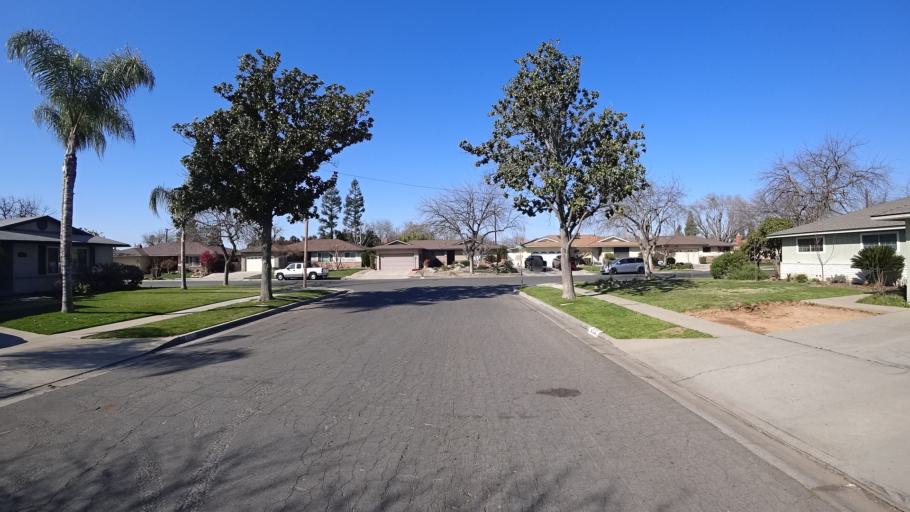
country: US
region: California
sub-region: Fresno County
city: Clovis
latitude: 36.8288
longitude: -119.7755
